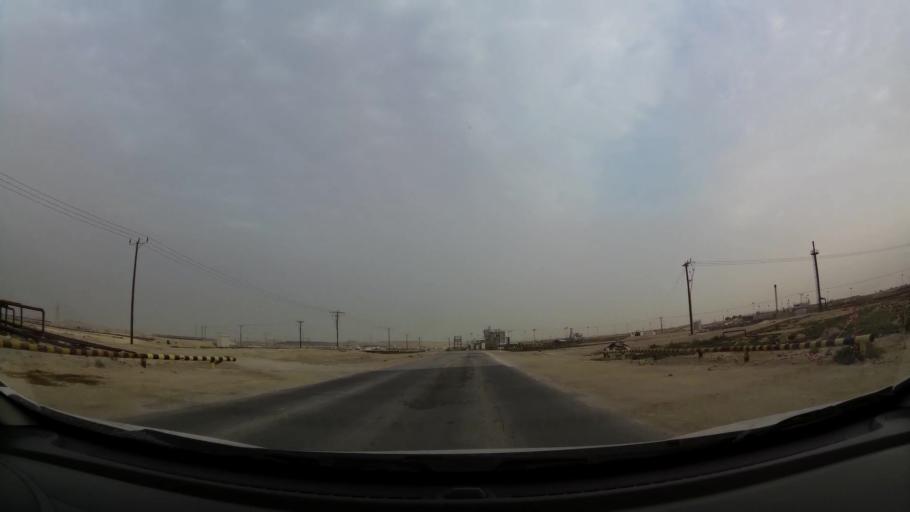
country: BH
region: Central Governorate
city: Dar Kulayb
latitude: 26.0187
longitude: 50.5734
